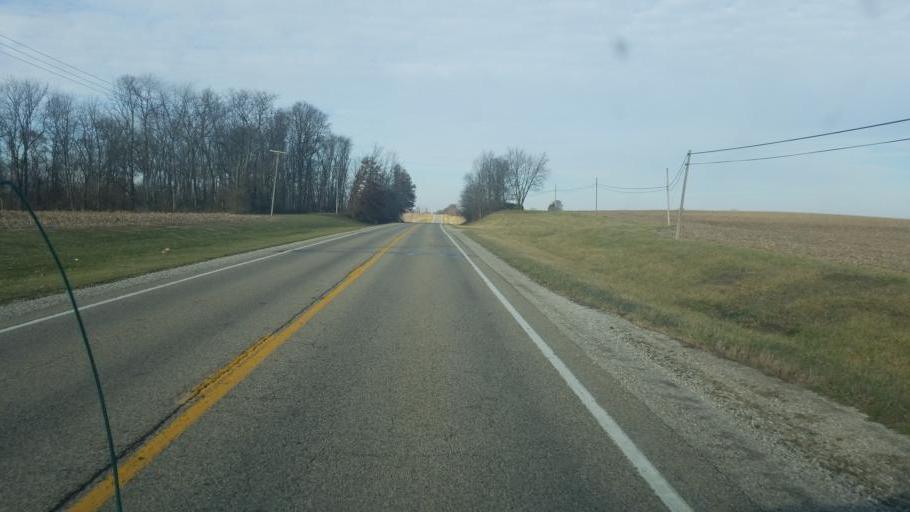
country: US
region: Illinois
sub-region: Lawrence County
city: Bridgeport
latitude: 38.6194
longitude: -87.6942
